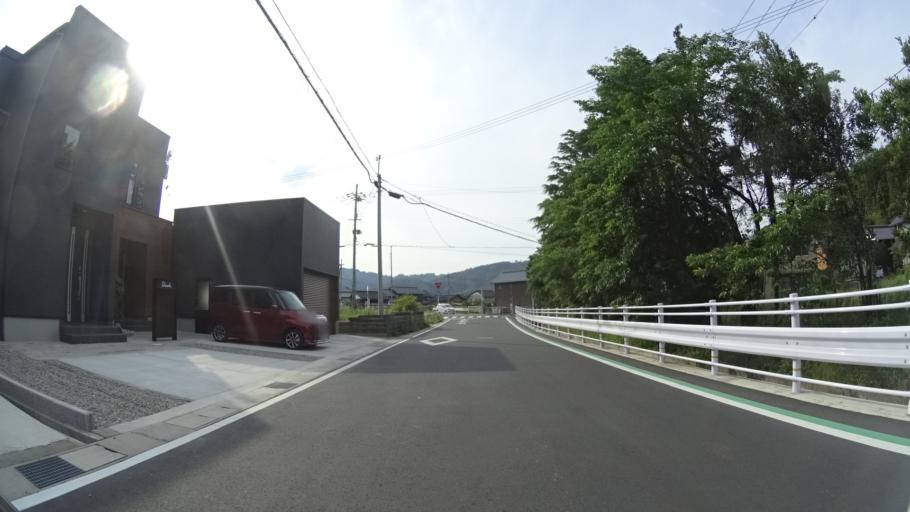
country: JP
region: Kyoto
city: Miyazu
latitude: 35.5308
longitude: 135.1252
